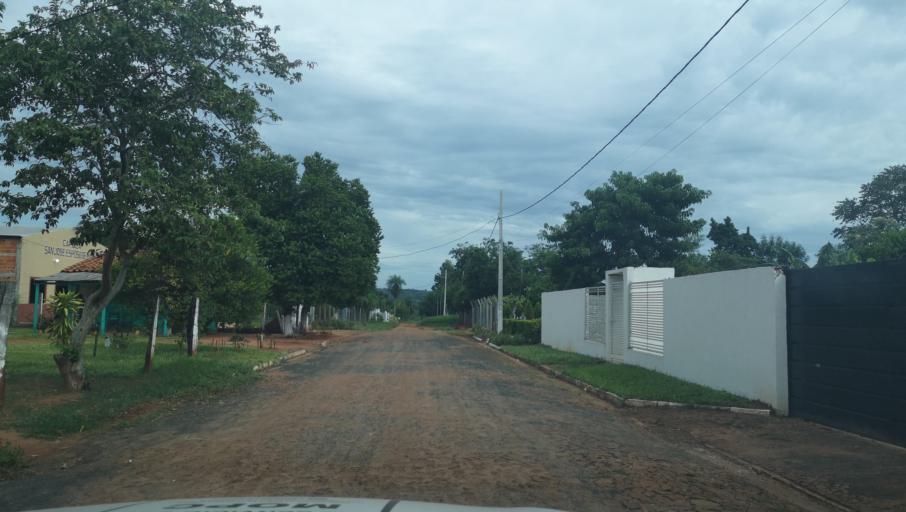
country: PY
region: San Pedro
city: Capiibary
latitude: -24.7264
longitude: -56.0222
